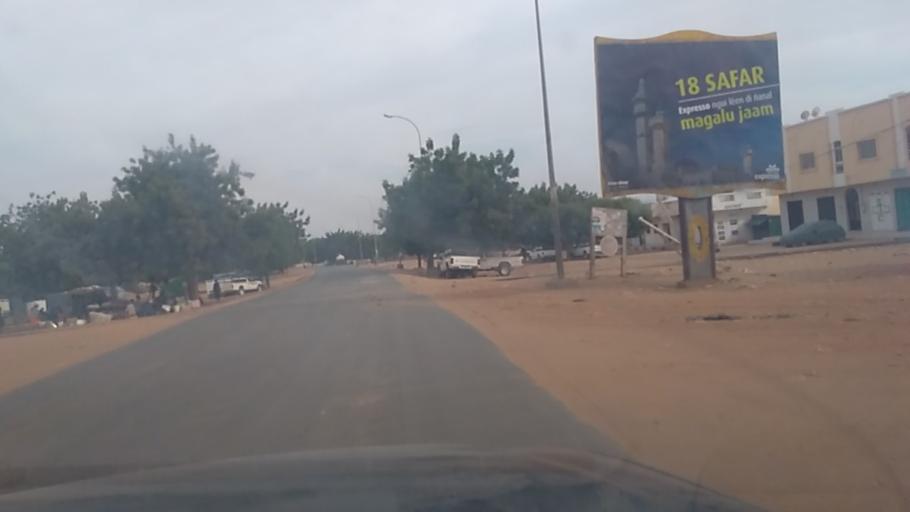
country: SN
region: Diourbel
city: Touba
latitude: 14.8396
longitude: -15.8823
